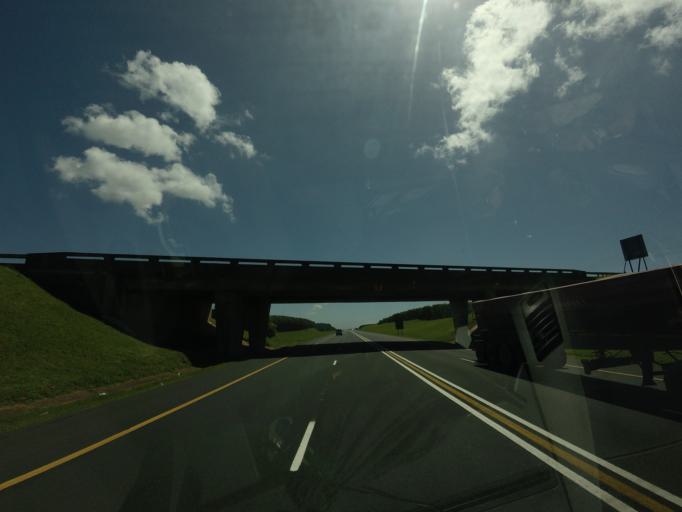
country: ZA
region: KwaZulu-Natal
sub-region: uThungulu District Municipality
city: Eshowe
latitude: -29.0412
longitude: 31.6483
